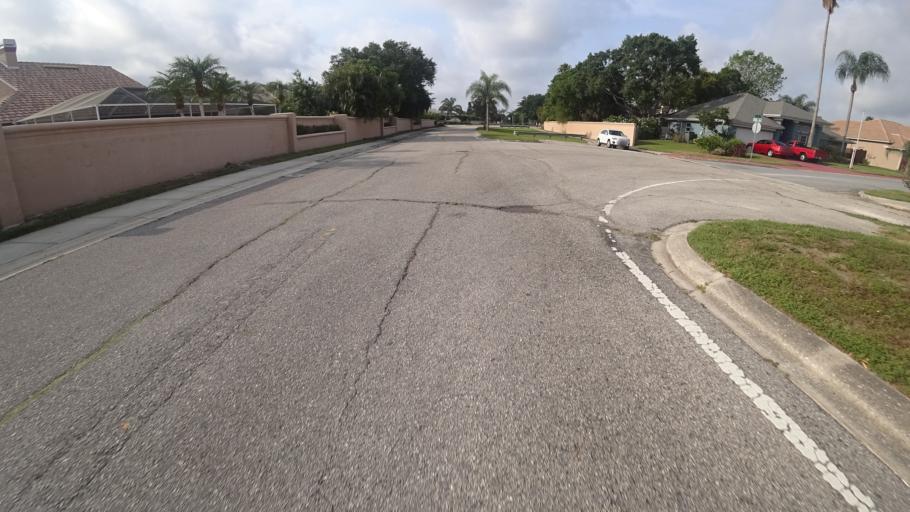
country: US
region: Florida
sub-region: Sarasota County
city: North Sarasota
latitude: 27.4143
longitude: -82.5134
